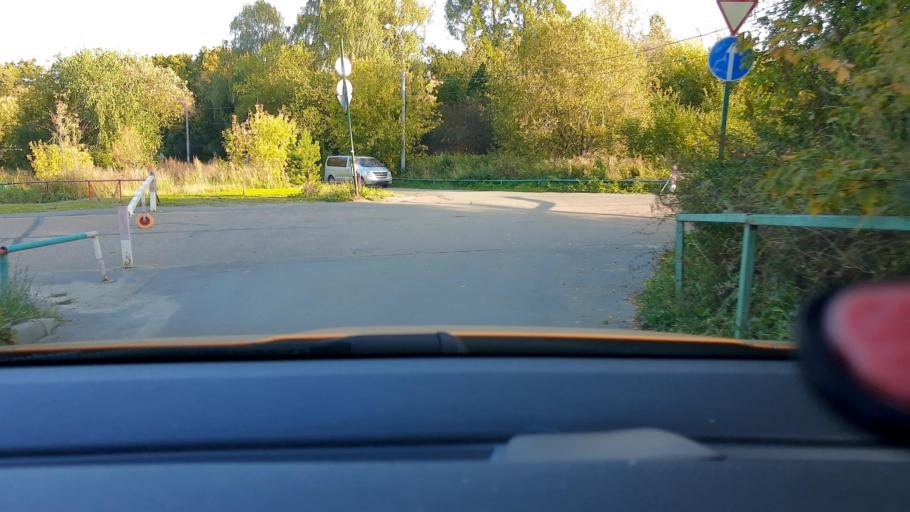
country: RU
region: Moskovskaya
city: Bol'shaya Setun'
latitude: 55.7560
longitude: 37.4228
